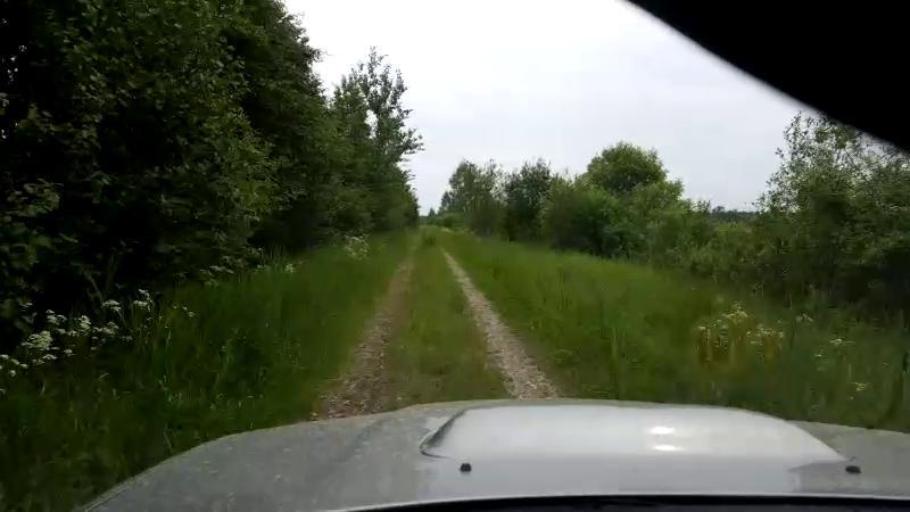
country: EE
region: Paernumaa
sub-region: Tootsi vald
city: Tootsi
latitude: 58.5658
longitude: 24.6891
